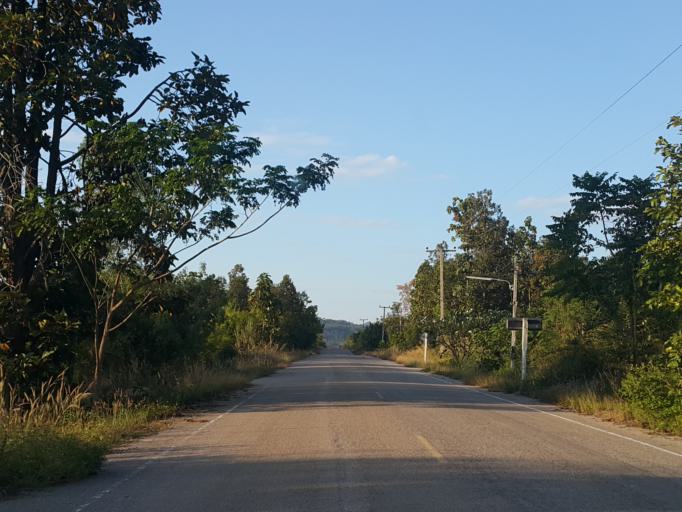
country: TH
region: Lampang
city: Lampang
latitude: 18.4270
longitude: 99.5724
